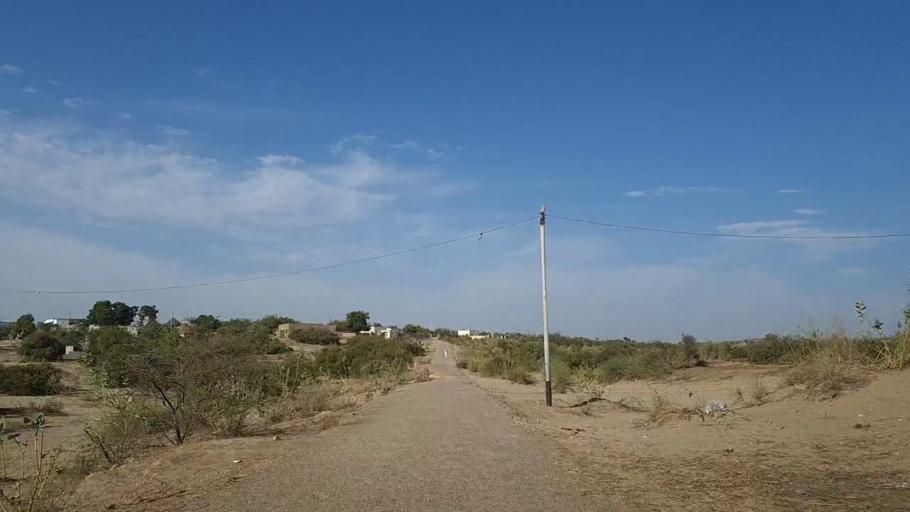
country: PK
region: Sindh
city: Naukot
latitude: 24.8639
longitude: 69.5282
